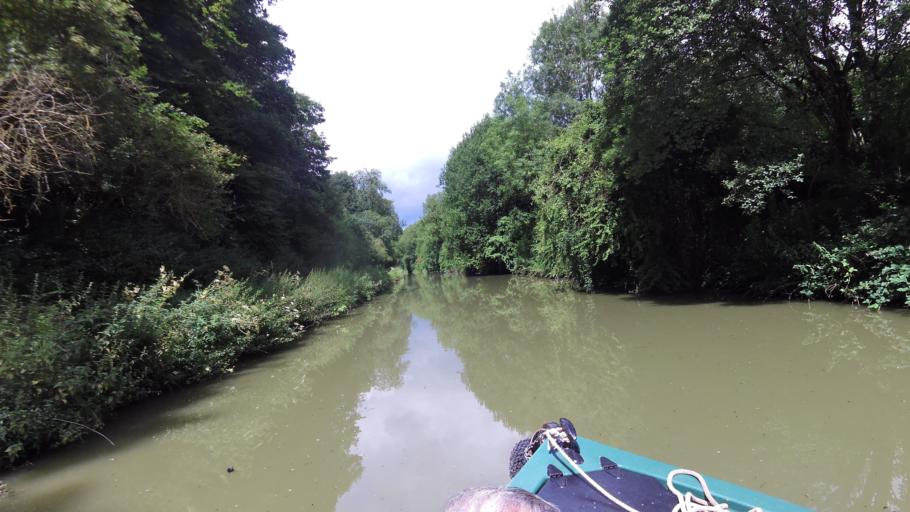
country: GB
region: England
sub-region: Wiltshire
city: Burbage
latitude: 51.3653
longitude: -1.6563
